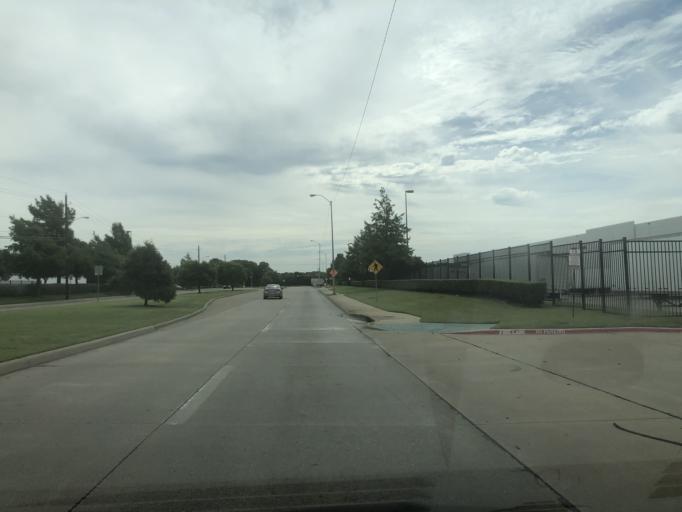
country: US
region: Texas
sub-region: Dallas County
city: Irving
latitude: 32.7984
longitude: -96.9978
